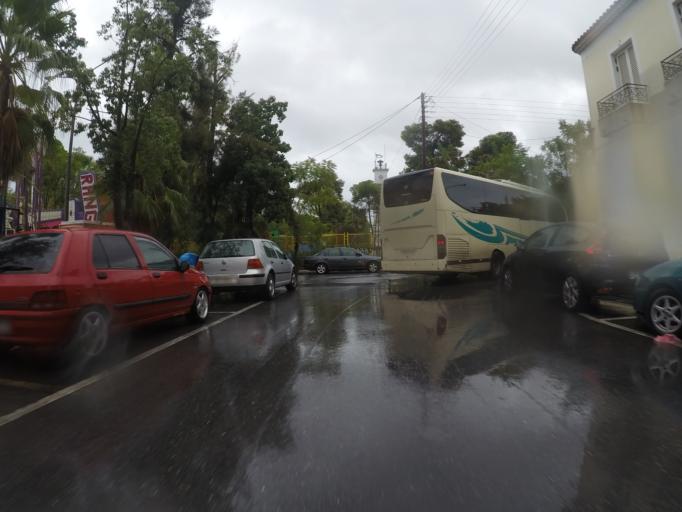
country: GR
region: Peloponnese
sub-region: Nomos Messinias
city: Messini
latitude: 37.0524
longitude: 22.0080
